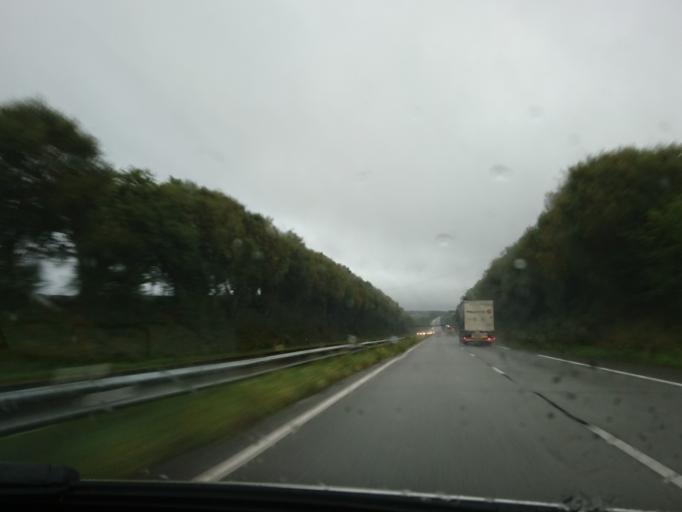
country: FR
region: Brittany
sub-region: Departement du Finistere
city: Briec
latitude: 48.1456
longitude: -4.0329
